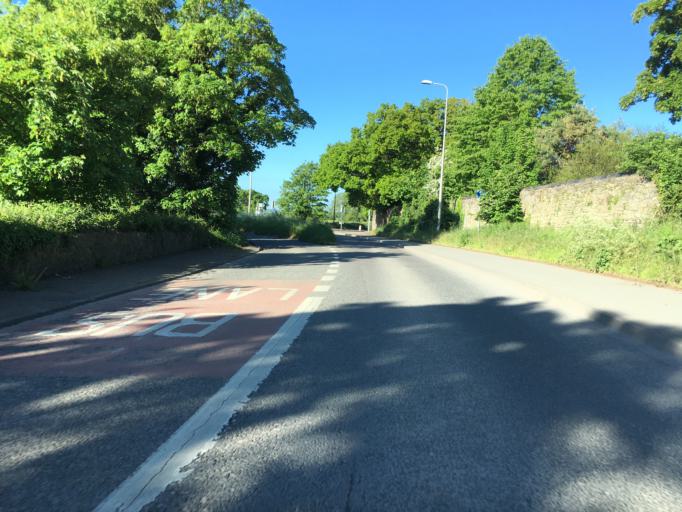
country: GB
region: England
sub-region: North Somerset
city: Long Ashton
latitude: 51.4385
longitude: -2.6369
